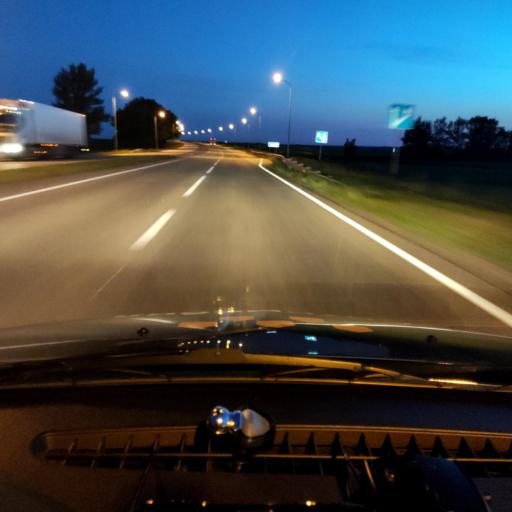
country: RU
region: Belgorod
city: Skorodnoye
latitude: 51.1735
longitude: 37.3262
